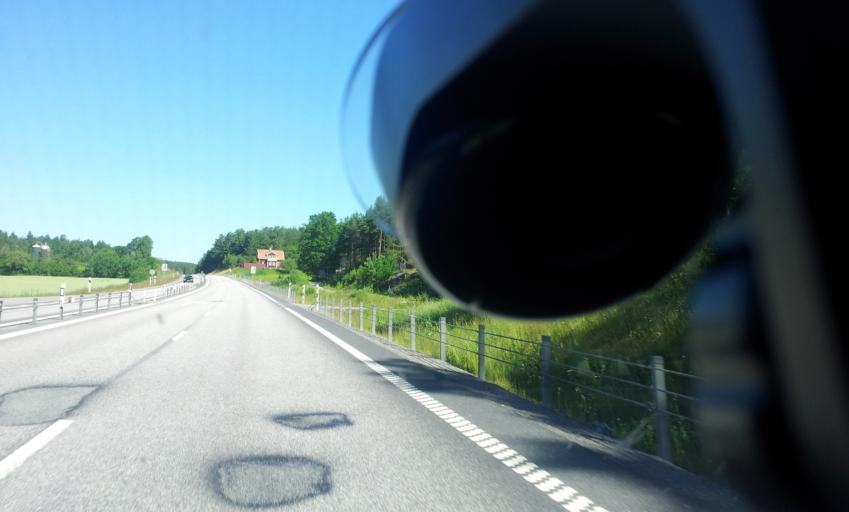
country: SE
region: OEstergoetland
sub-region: Soderkopings Kommun
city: Soederkoeping
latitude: 58.4190
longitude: 16.3969
